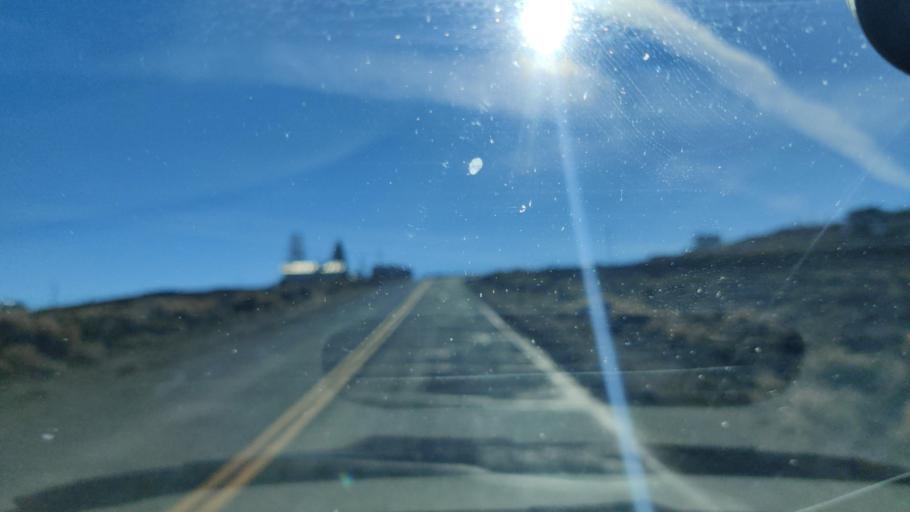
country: US
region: Colorado
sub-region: Gunnison County
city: Gunnison
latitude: 38.5457
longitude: -106.9550
